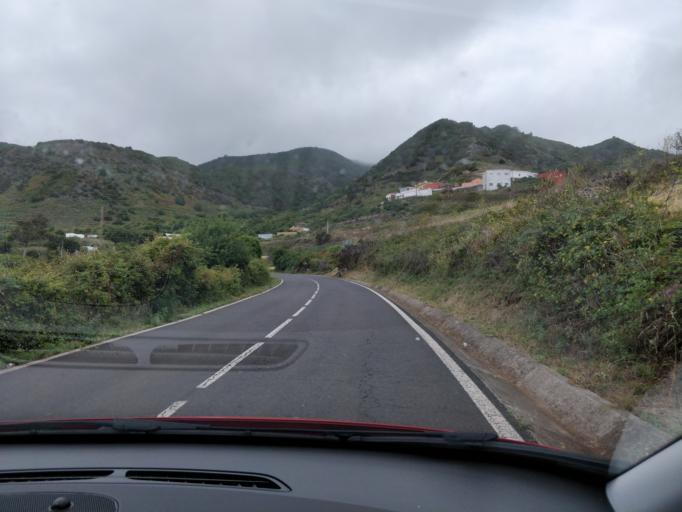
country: ES
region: Canary Islands
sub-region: Provincia de Santa Cruz de Tenerife
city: Tanque
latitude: 28.3343
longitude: -16.8465
